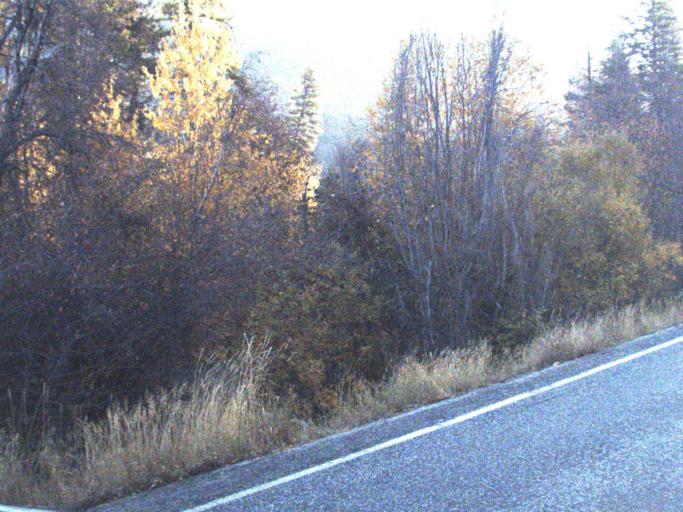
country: US
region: Washington
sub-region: Ferry County
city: Republic
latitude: 48.2680
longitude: -118.7005
